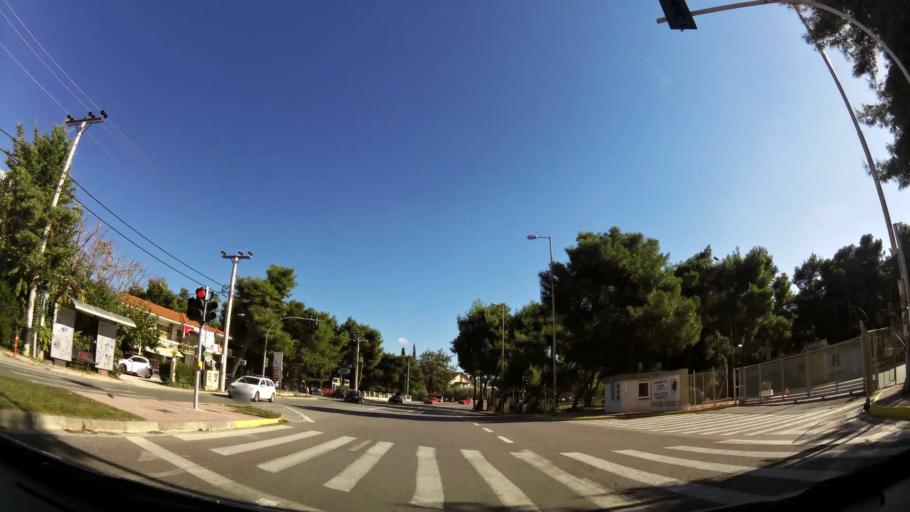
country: GR
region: Attica
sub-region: Nomarchia Anatolikis Attikis
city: Drosia
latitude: 38.1226
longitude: 23.8576
